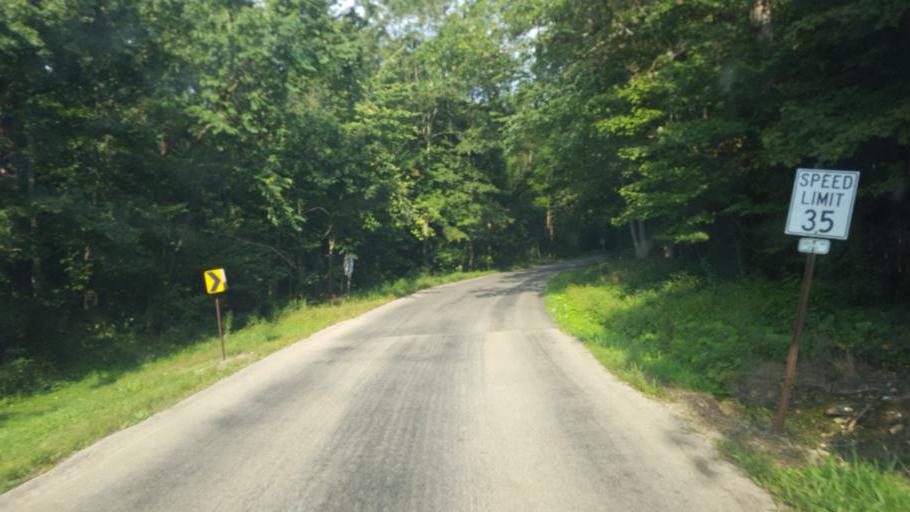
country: US
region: Ohio
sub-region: Knox County
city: Gambier
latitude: 40.3719
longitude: -82.4201
